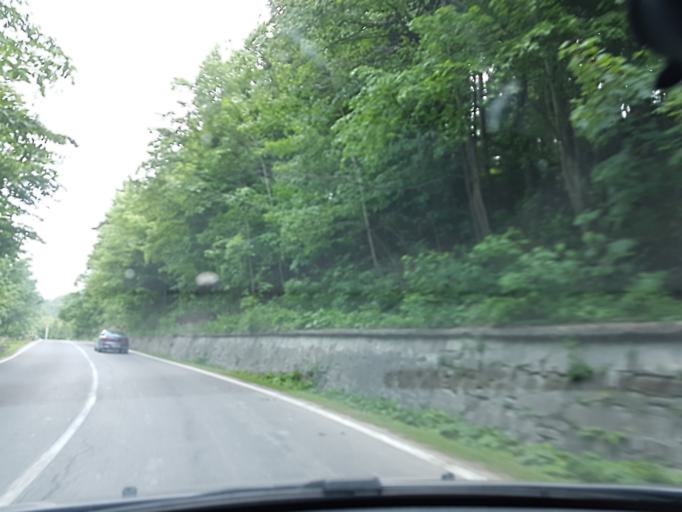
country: RO
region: Prahova
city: Maneciu
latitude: 45.3684
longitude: 25.9295
